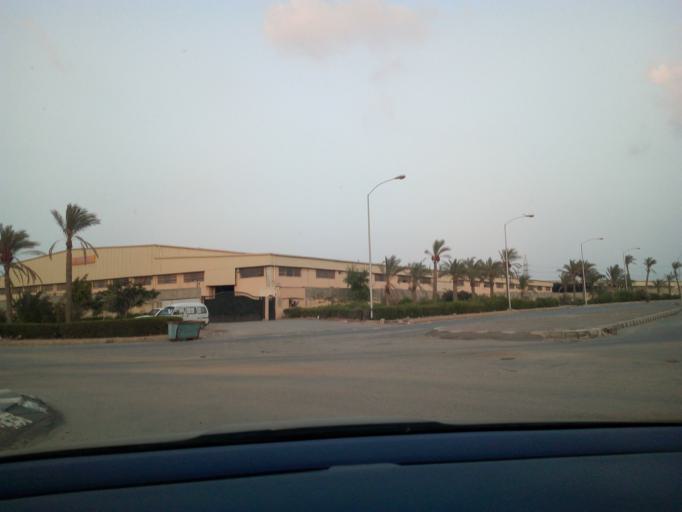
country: EG
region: Eastern Province
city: Bilbays
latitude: 30.2473
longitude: 31.7595
